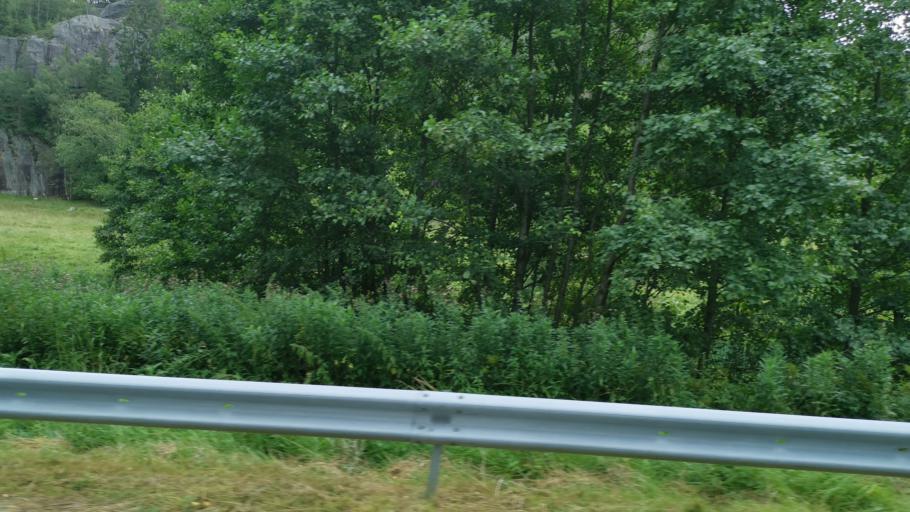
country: SE
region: Vaestra Goetaland
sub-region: Lysekils Kommun
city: Brastad
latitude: 58.4742
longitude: 11.4187
